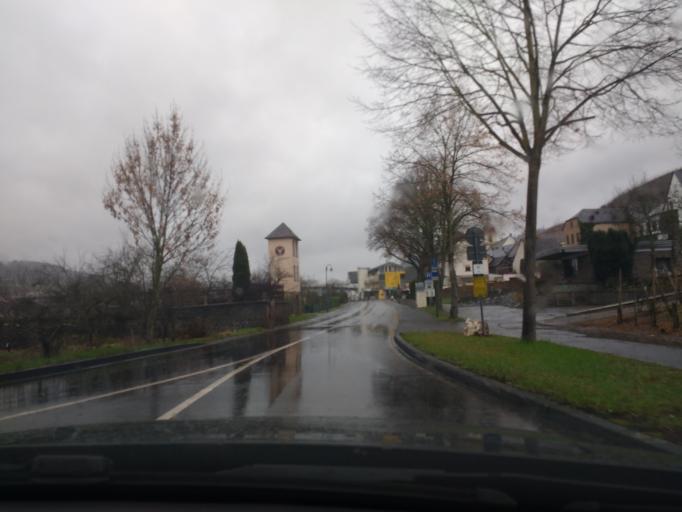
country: DE
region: Rheinland-Pfalz
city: Kinheim
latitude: 49.9719
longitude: 7.0594
